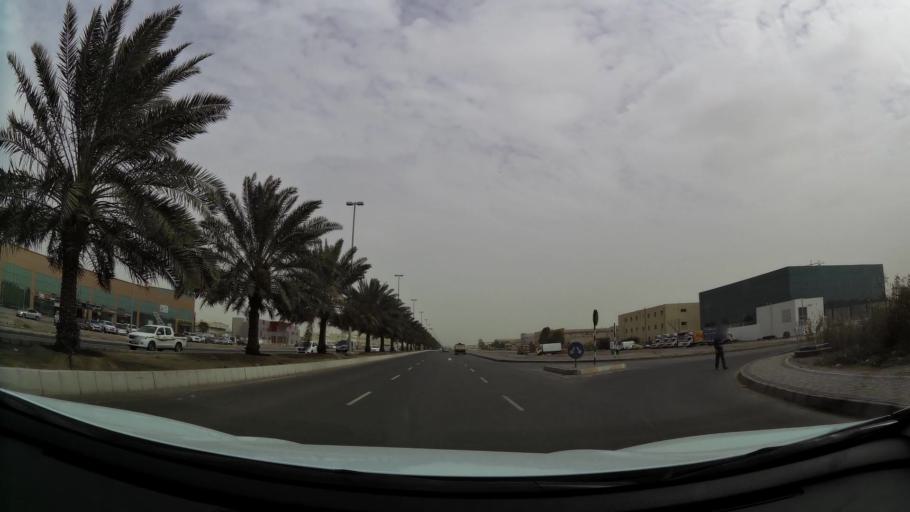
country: AE
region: Abu Dhabi
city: Abu Dhabi
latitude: 24.3446
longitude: 54.4749
